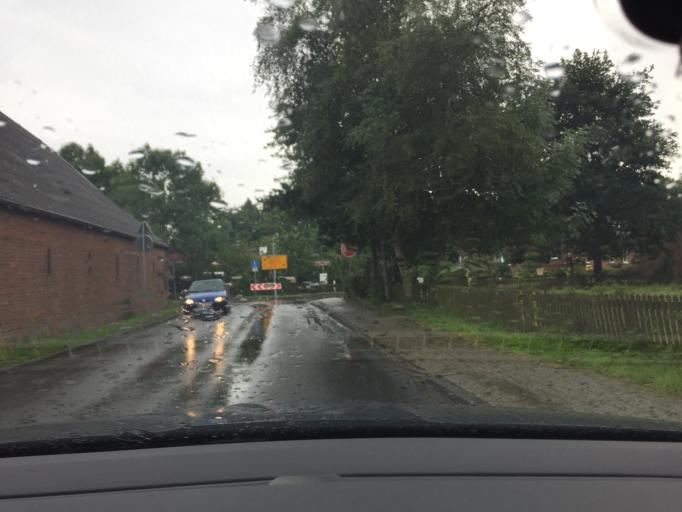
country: DE
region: Lower Saxony
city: Hinte
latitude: 53.4348
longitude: 7.0681
